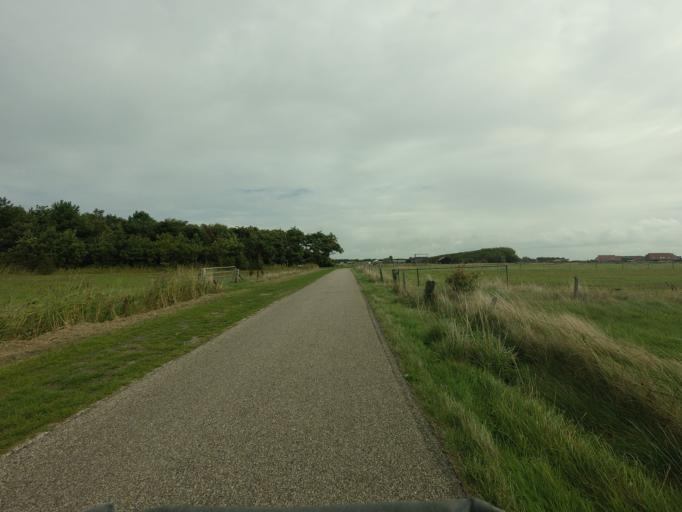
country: NL
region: Friesland
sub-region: Gemeente Ameland
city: Nes
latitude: 53.4526
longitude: 5.7943
